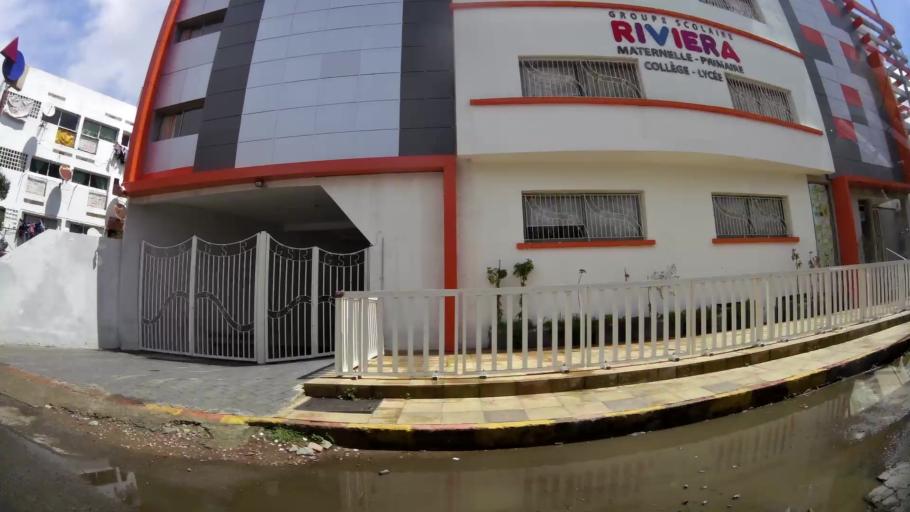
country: MA
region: Grand Casablanca
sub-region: Casablanca
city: Casablanca
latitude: 33.5691
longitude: -7.6385
